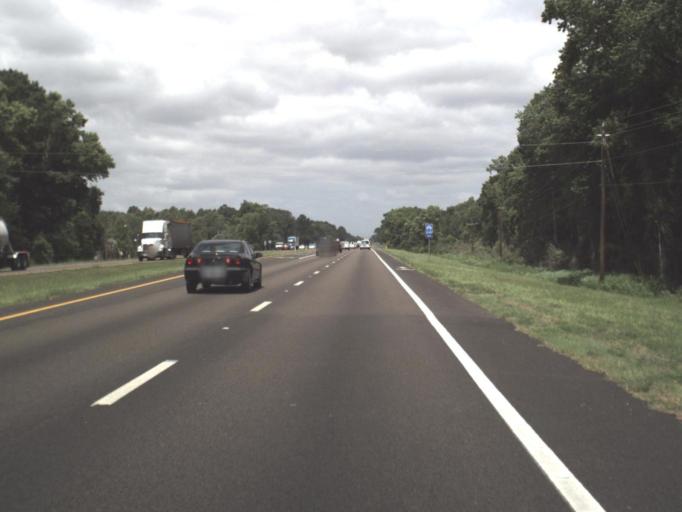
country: US
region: Florida
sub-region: Nassau County
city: Yulee
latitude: 30.6295
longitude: -81.5673
